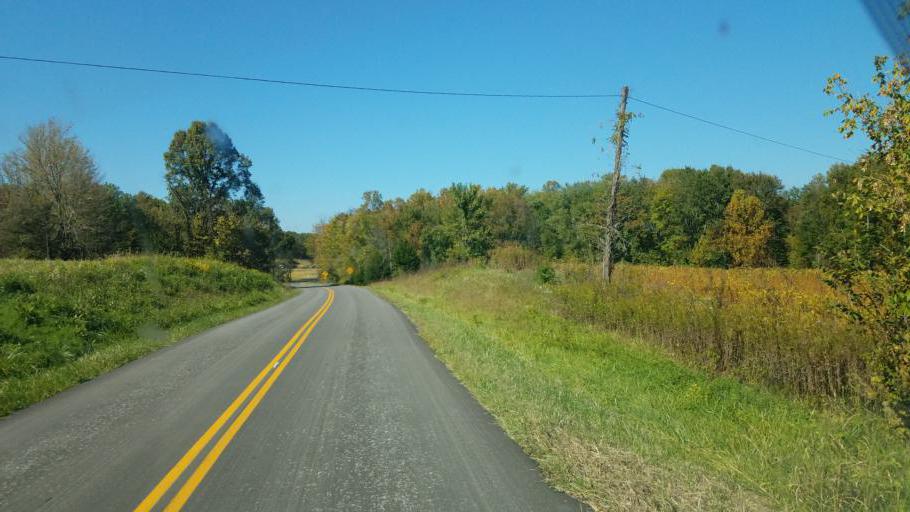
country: US
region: Kentucky
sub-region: Fleming County
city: Flemingsburg
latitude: 38.4452
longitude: -83.5808
